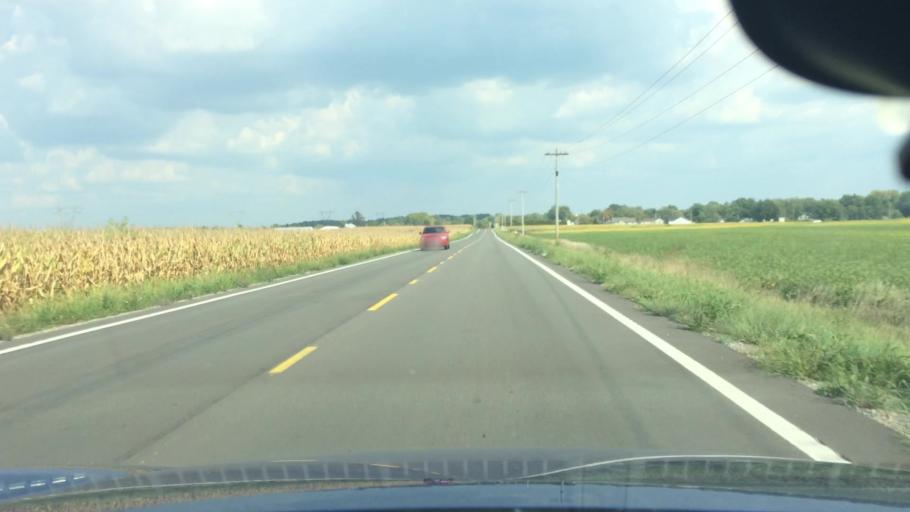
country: US
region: Ohio
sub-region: Logan County
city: Russells Point
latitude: 40.4462
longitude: -83.8161
